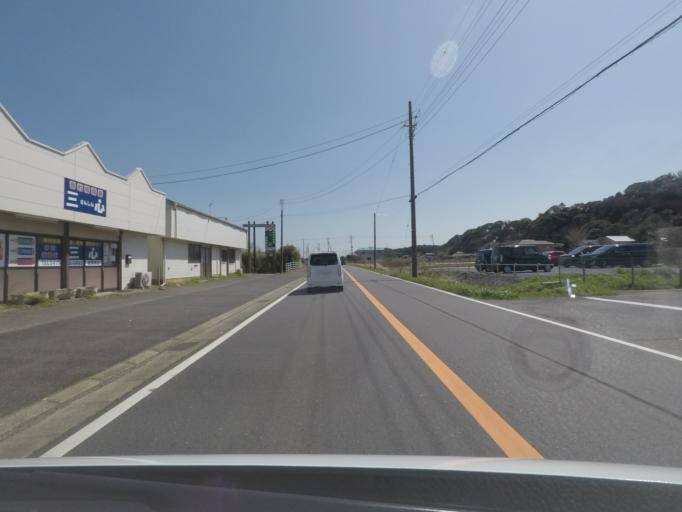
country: JP
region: Chiba
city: Omigawa
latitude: 35.8058
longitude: 140.7103
